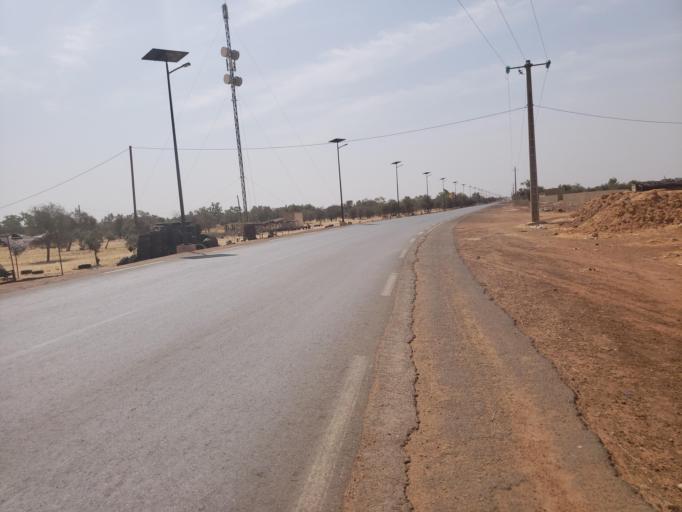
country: SN
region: Matam
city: Ranerou
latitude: 15.2950
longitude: -13.9579
